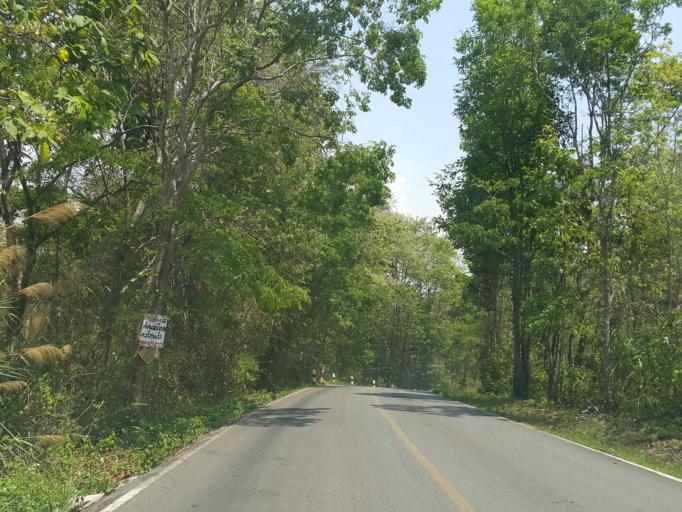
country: TH
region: Chiang Mai
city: Mae On
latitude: 18.9050
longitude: 99.2529
